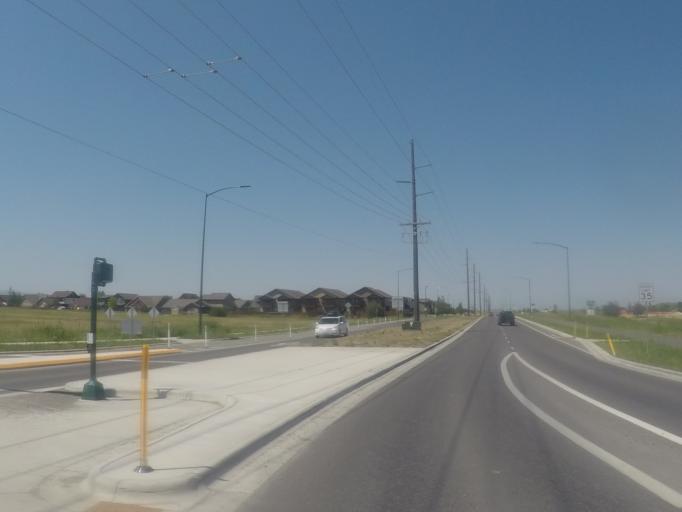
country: US
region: Montana
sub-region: Gallatin County
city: Bozeman
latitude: 45.6930
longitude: -111.0834
